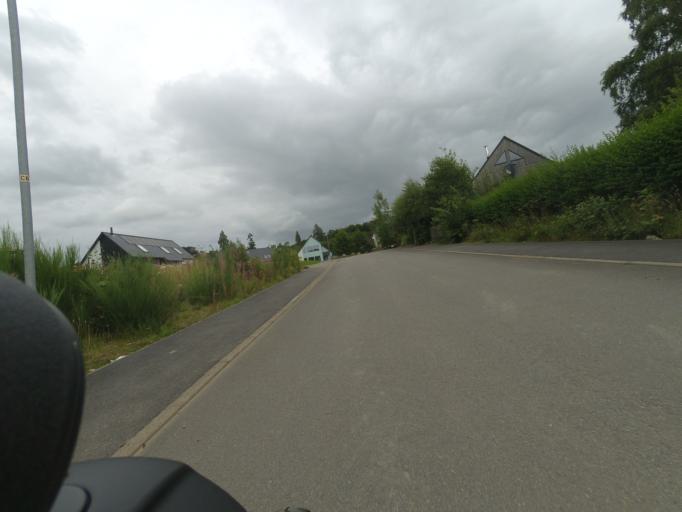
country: GB
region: Scotland
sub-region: Highland
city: Muir of Ord
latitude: 57.5703
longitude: -4.5770
